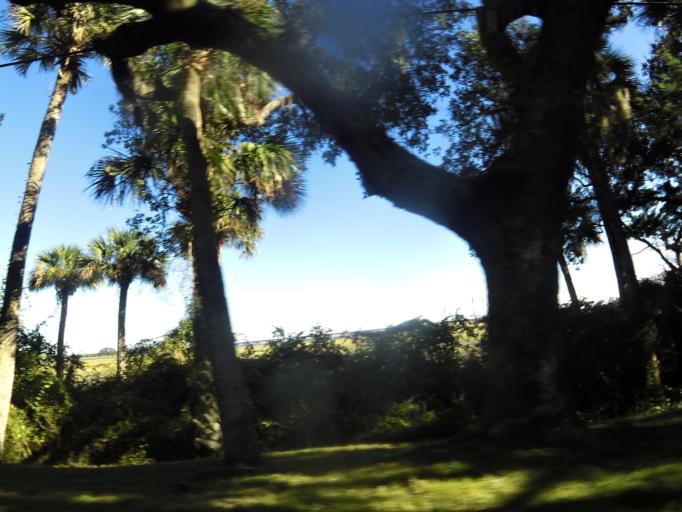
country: US
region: Florida
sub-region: Duval County
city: Atlantic Beach
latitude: 30.4244
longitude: -81.4277
